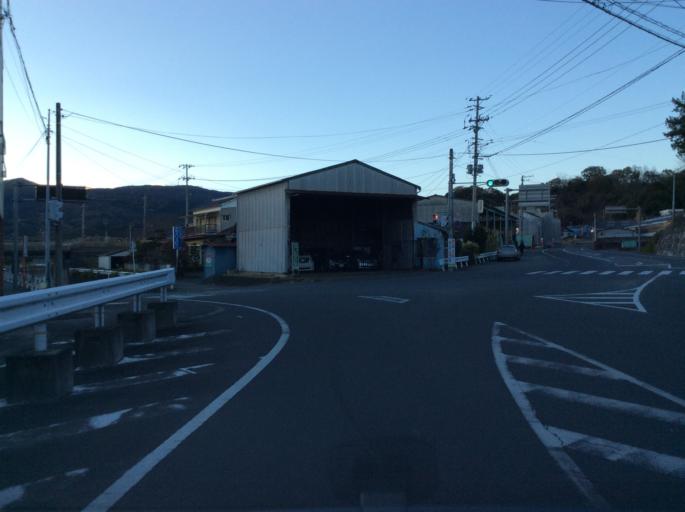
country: JP
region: Fukushima
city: Iwaki
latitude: 37.0867
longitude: 140.8628
